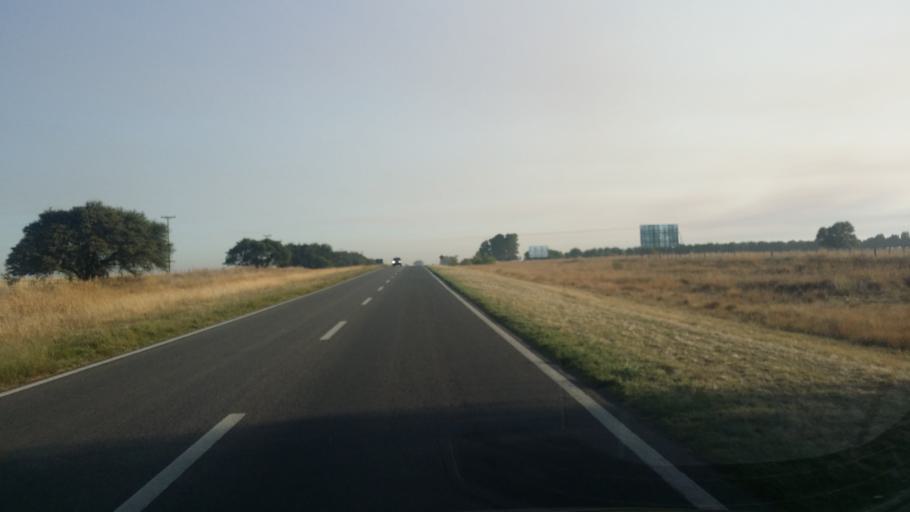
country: AR
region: La Pampa
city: Santa Rosa
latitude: -36.5082
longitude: -64.2802
